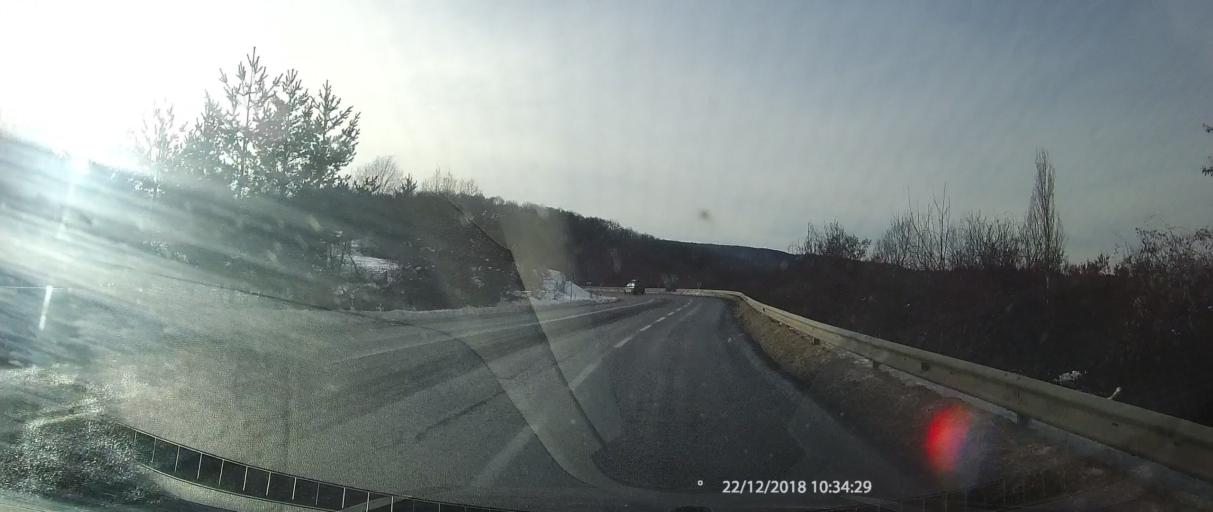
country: MK
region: Kriva Palanka
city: Kriva Palanka
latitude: 42.2179
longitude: 22.4505
